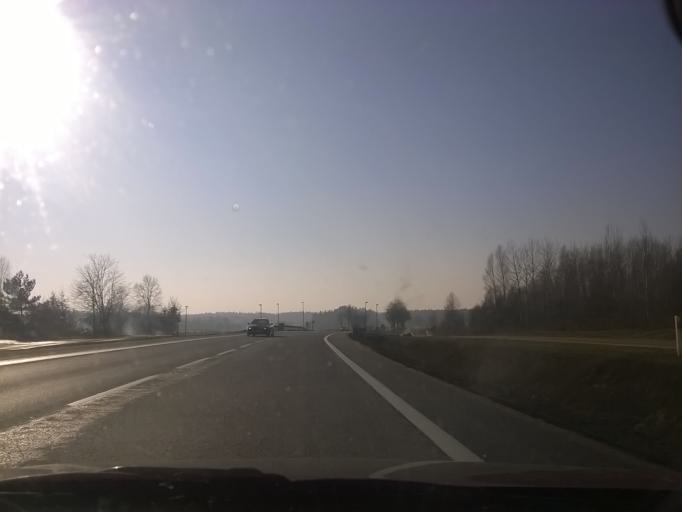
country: PL
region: Warmian-Masurian Voivodeship
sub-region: Powiat olsztynski
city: Barczewo
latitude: 53.8097
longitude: 20.6325
